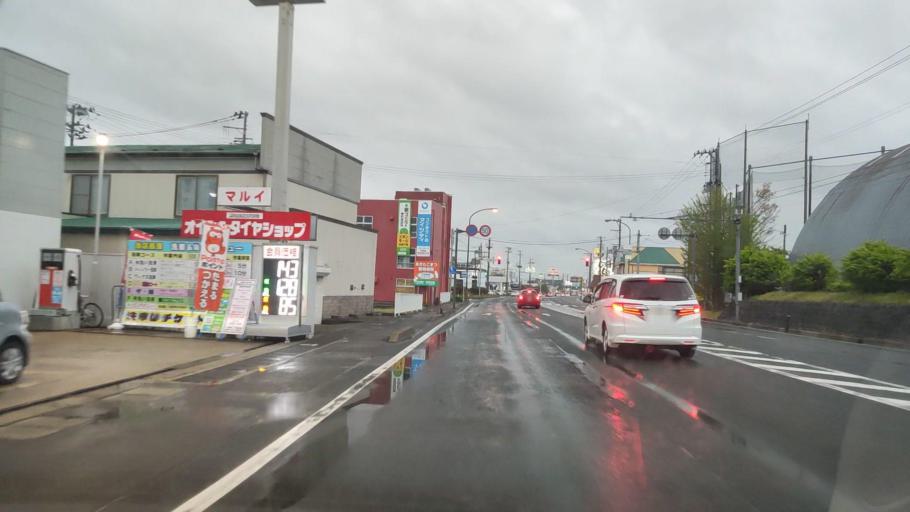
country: JP
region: Akita
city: Akita
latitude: 39.6909
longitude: 140.1227
